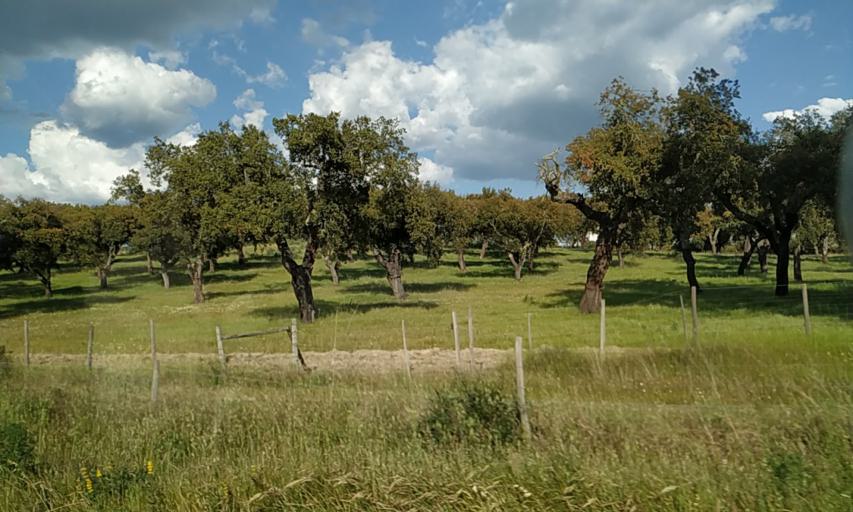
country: PT
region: Portalegre
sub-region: Portalegre
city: Urra
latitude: 39.2221
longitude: -7.4570
